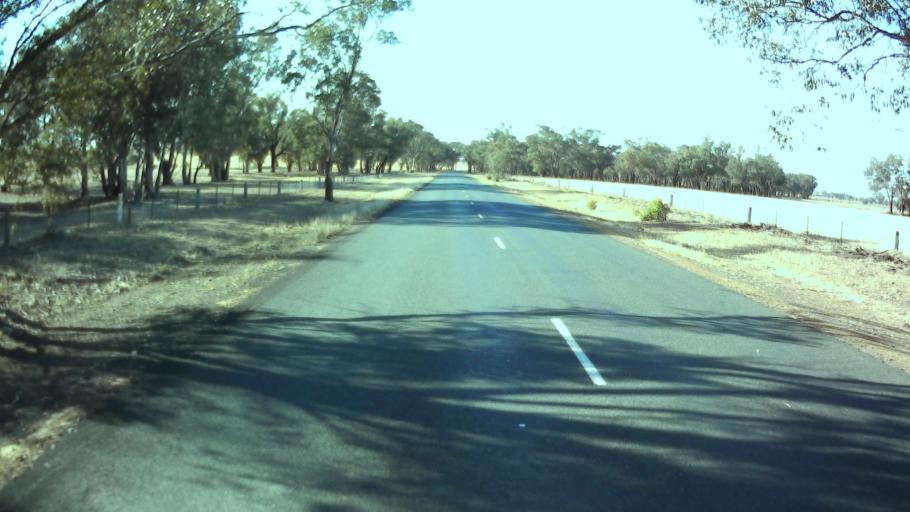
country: AU
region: New South Wales
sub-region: Weddin
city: Grenfell
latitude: -33.9471
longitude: 148.1366
